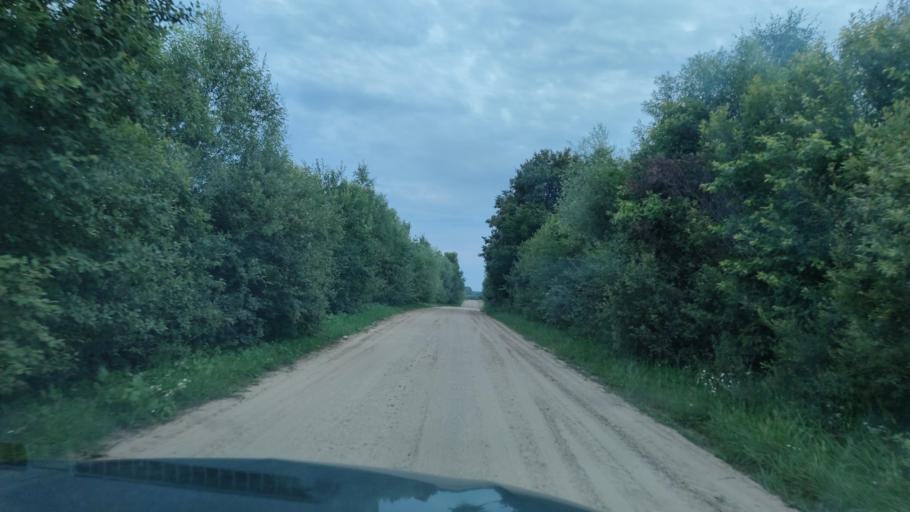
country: BY
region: Minsk
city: Myadzyel
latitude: 55.0923
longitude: 27.1315
